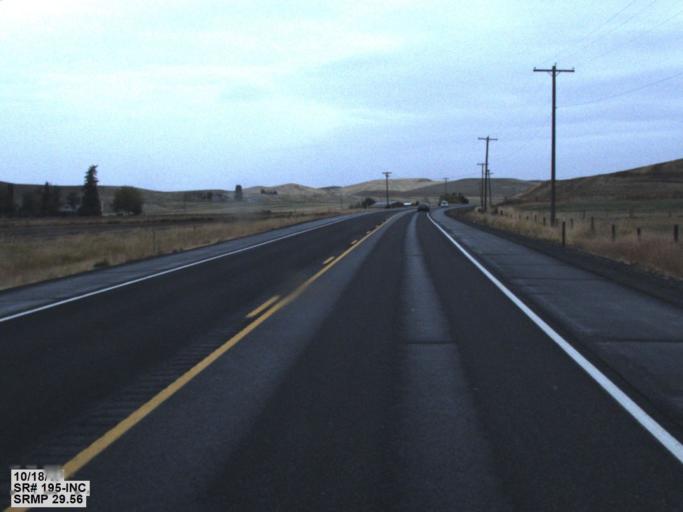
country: US
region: Washington
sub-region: Whitman County
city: Colfax
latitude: 46.7808
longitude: -117.2960
